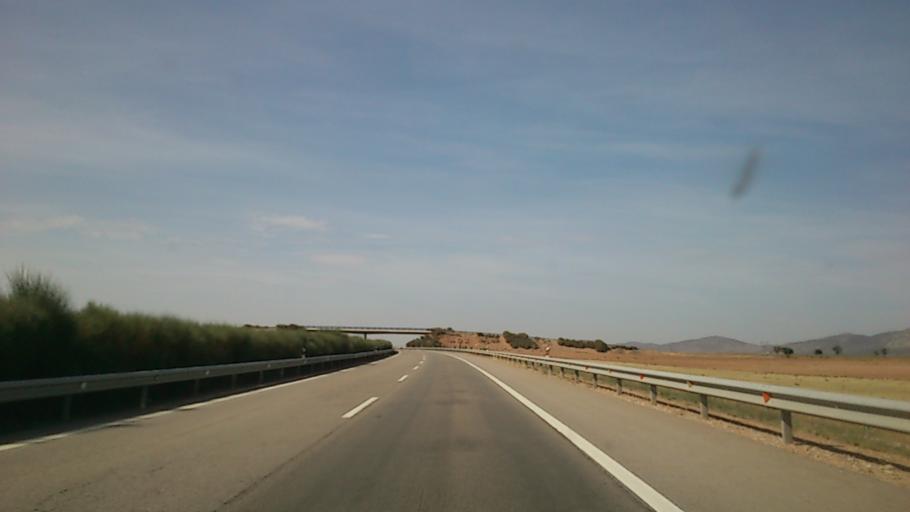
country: ES
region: Aragon
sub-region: Provincia de Teruel
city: Villarquemado
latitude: 40.5162
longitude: -1.2536
